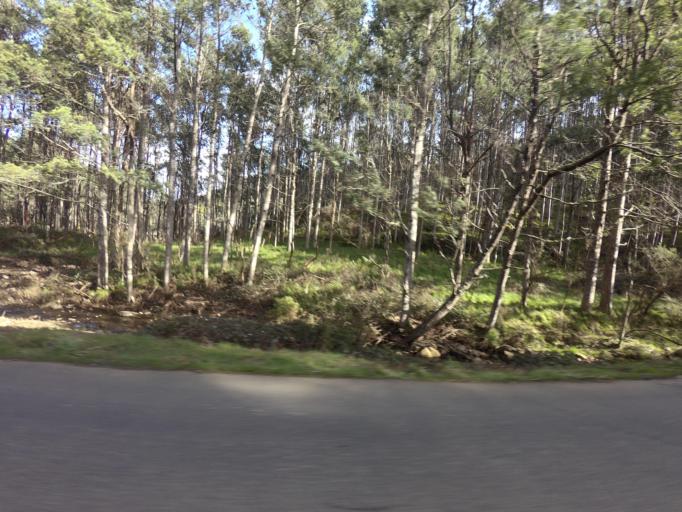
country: AU
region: Tasmania
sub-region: Huon Valley
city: Huonville
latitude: -43.0349
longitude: 147.1440
